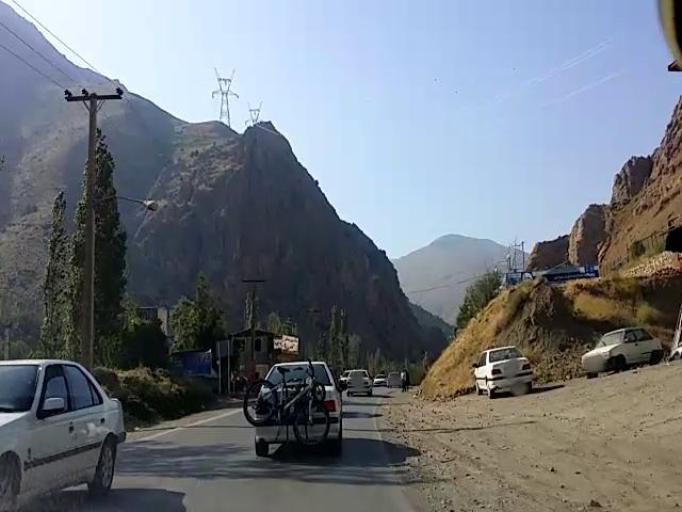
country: IR
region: Tehran
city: Tajrish
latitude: 36.0819
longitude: 51.3173
